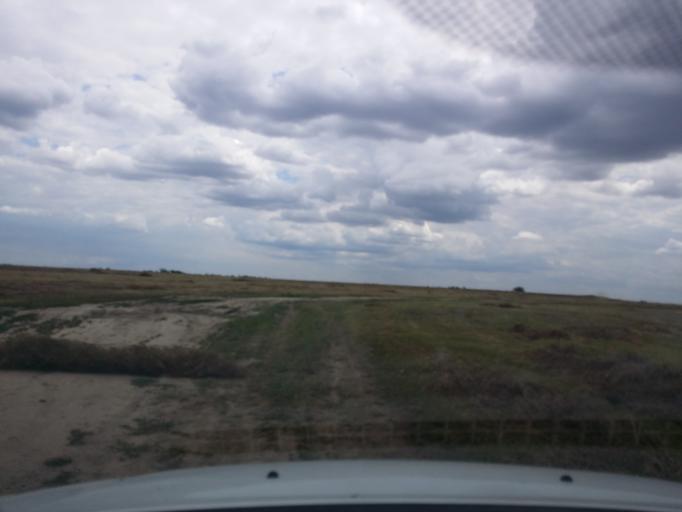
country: HU
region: Hajdu-Bihar
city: Egyek
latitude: 47.5646
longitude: 20.9445
